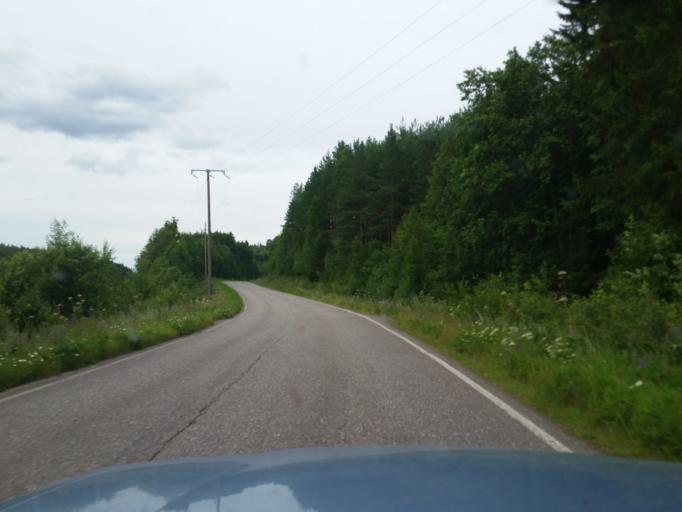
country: FI
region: Uusimaa
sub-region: Helsinki
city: Sammatti
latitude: 60.3929
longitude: 23.8139
